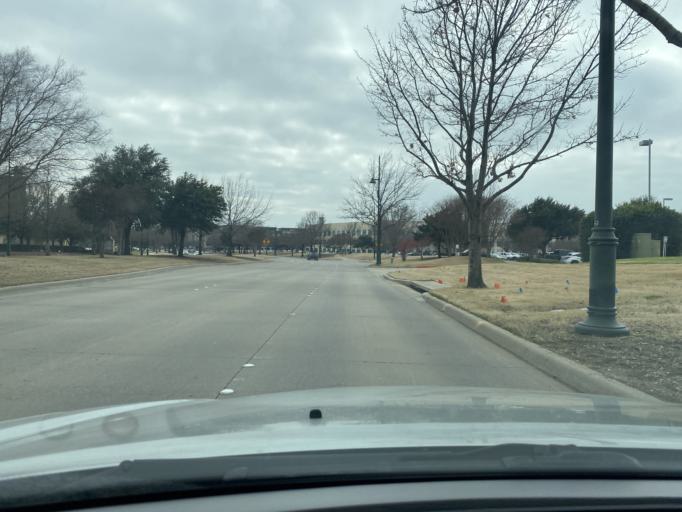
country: US
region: Texas
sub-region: Collin County
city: Frisco
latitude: 33.1098
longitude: -96.8165
